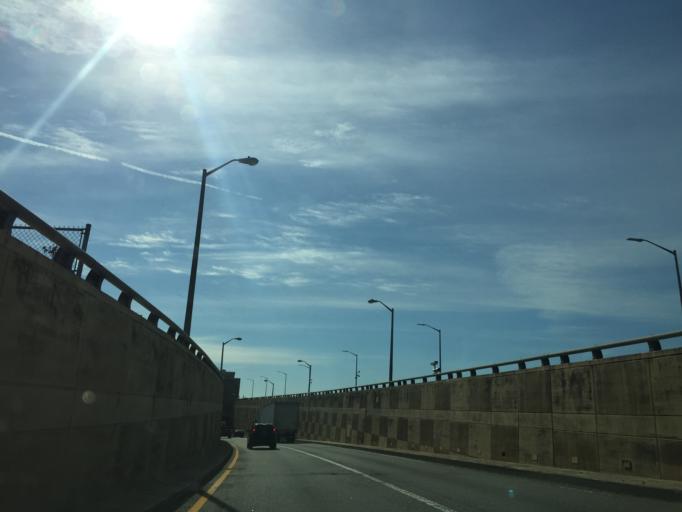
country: US
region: Virginia
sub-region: City of Hampton
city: East Hampton
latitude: 37.0020
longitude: -76.3196
